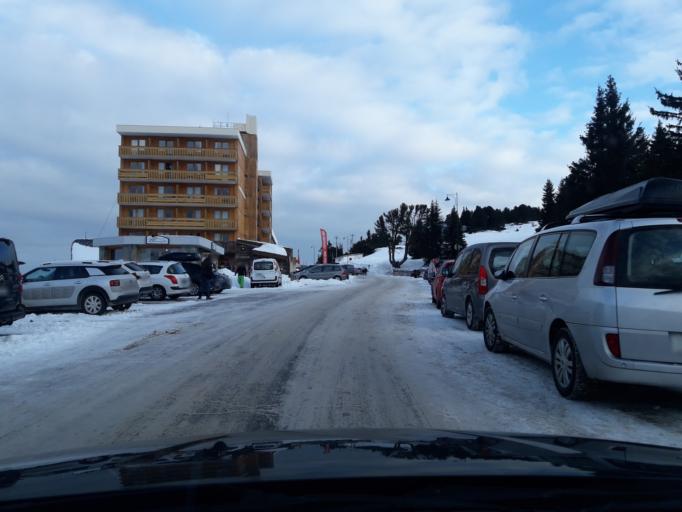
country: FR
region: Rhone-Alpes
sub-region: Departement de l'Isere
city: Vaulnaveys-le-Bas
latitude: 45.1130
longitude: 5.8785
